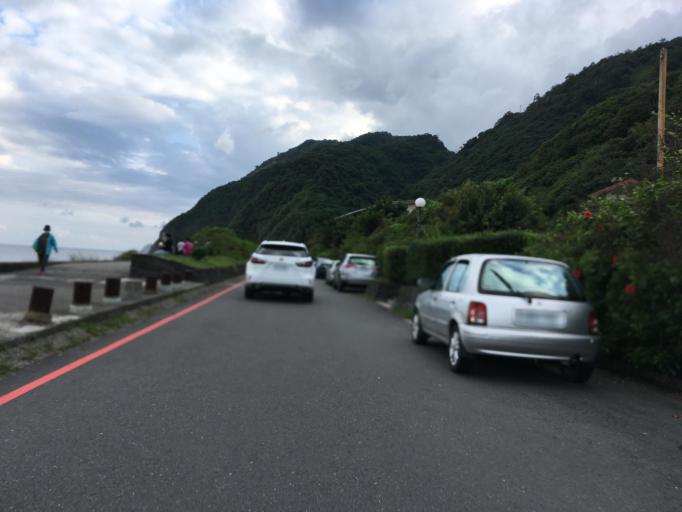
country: TW
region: Taiwan
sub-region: Yilan
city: Yilan
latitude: 24.5752
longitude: 121.8691
